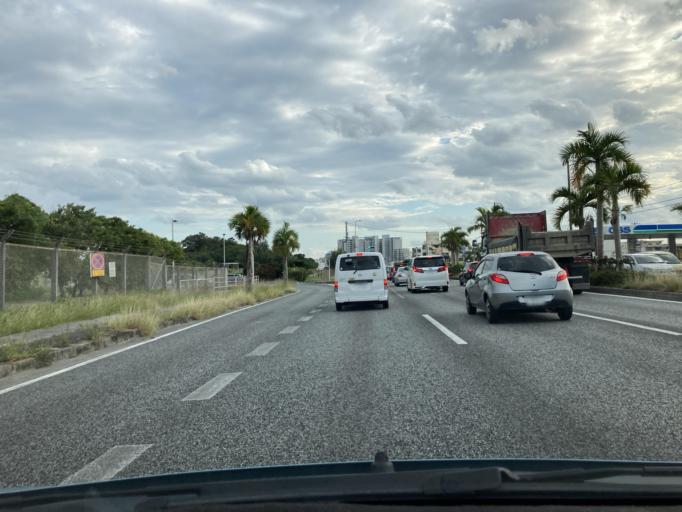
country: JP
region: Okinawa
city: Chatan
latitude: 26.3326
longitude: 127.7517
